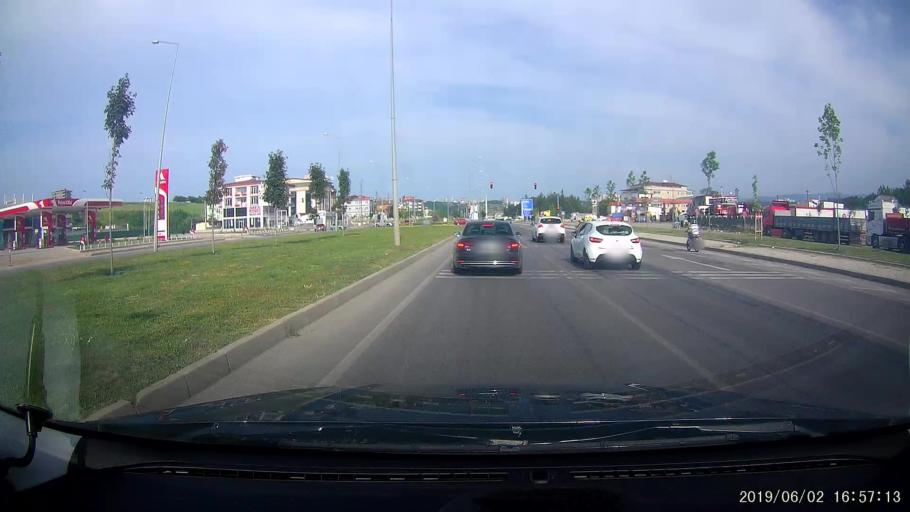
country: TR
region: Samsun
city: Samsun
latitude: 41.2910
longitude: 36.2728
